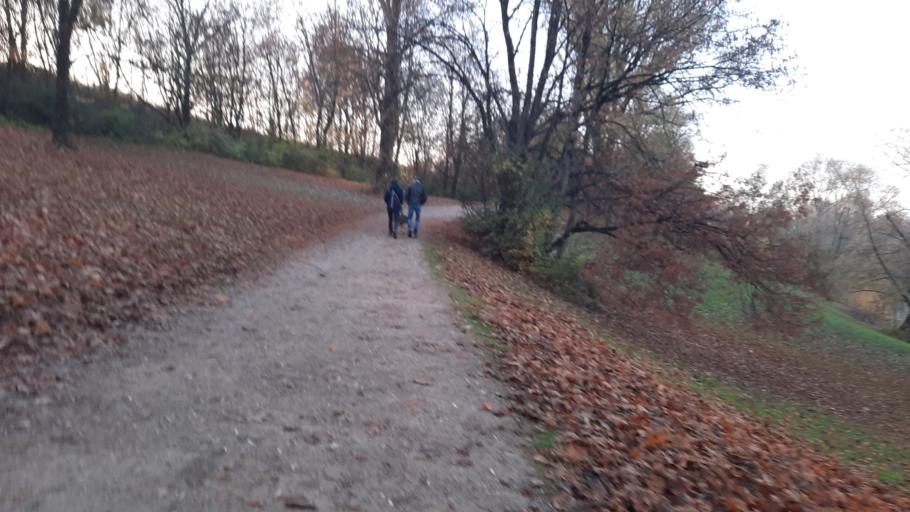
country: DE
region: Bavaria
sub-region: Upper Bavaria
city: Feldkirchen
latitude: 48.1547
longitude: 11.7369
